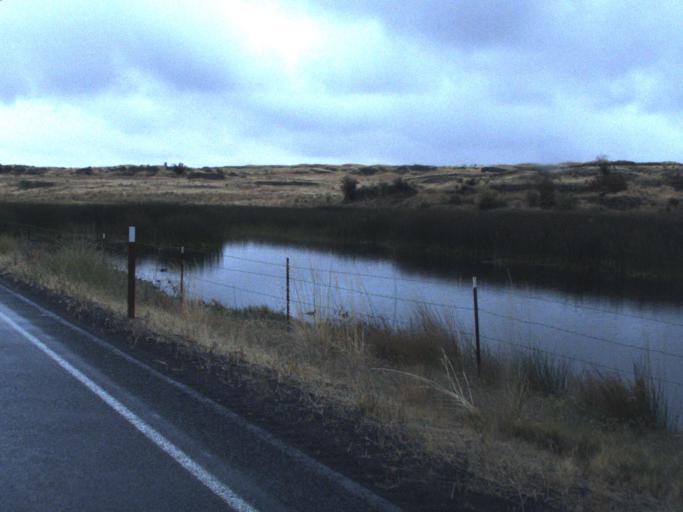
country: US
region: Washington
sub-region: Spokane County
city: Medical Lake
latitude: 47.2711
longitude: -117.9470
